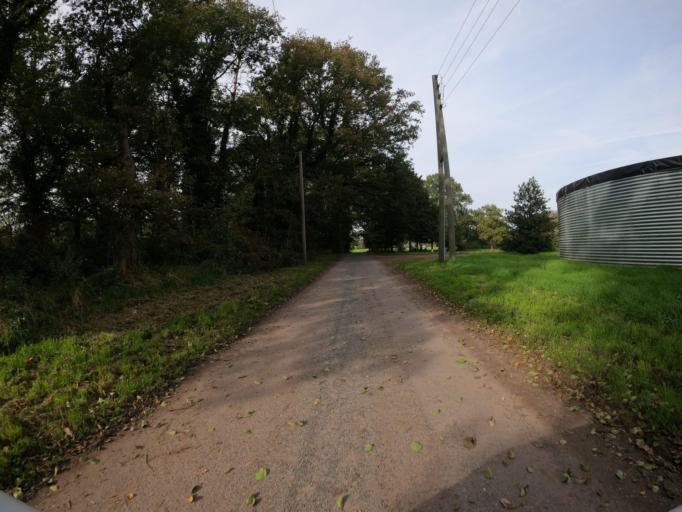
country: DE
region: North Rhine-Westphalia
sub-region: Regierungsbezirk Dusseldorf
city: Schermbeck
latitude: 51.7030
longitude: 6.8554
